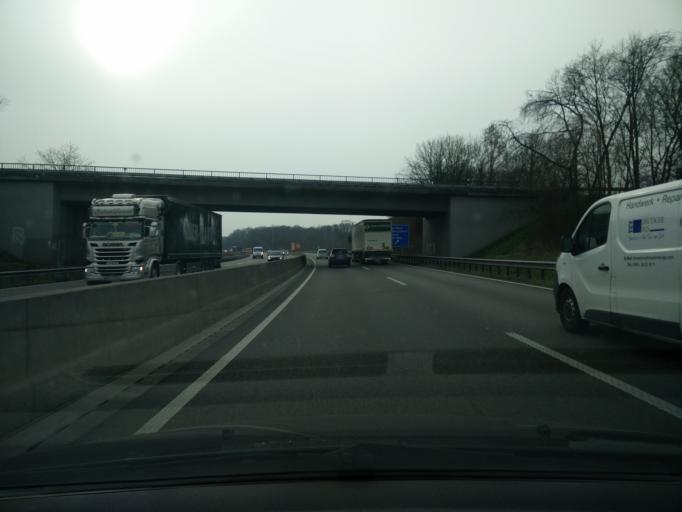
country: DE
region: Rheinland-Pfalz
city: Kandel
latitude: 49.1048
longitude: 8.1818
